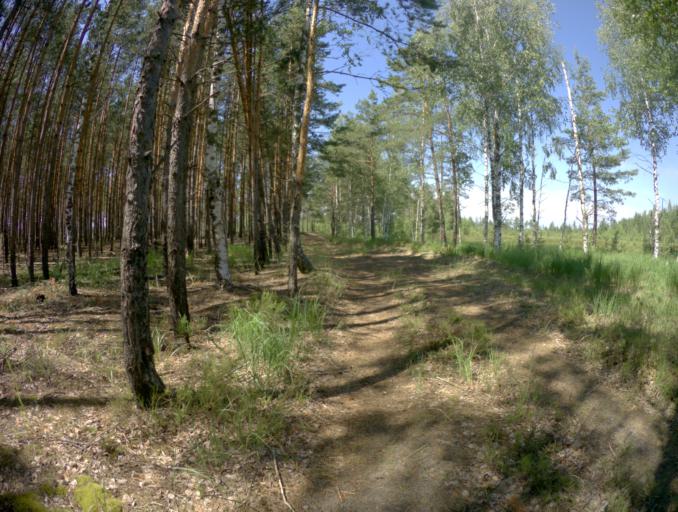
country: RU
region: Ivanovo
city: Talitsy
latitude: 56.4356
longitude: 42.2622
